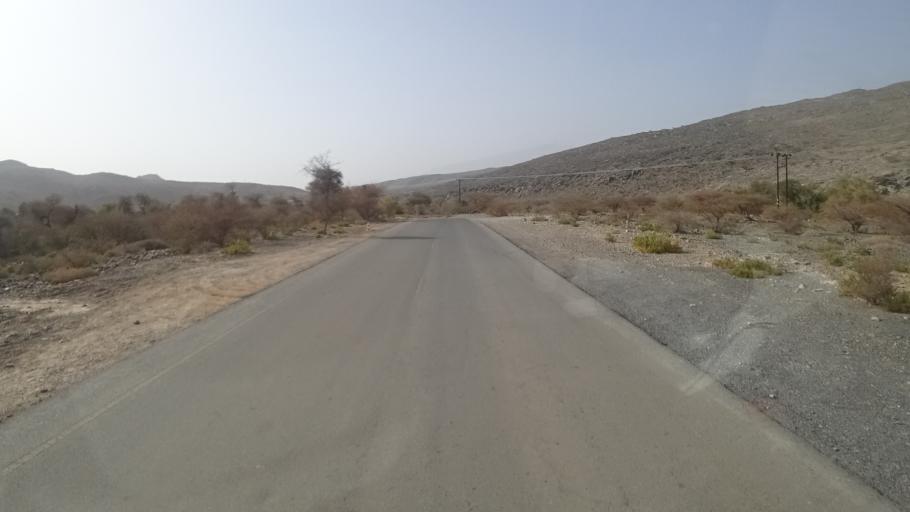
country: OM
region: Muhafazat ad Dakhiliyah
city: Bahla'
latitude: 23.0657
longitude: 57.3760
